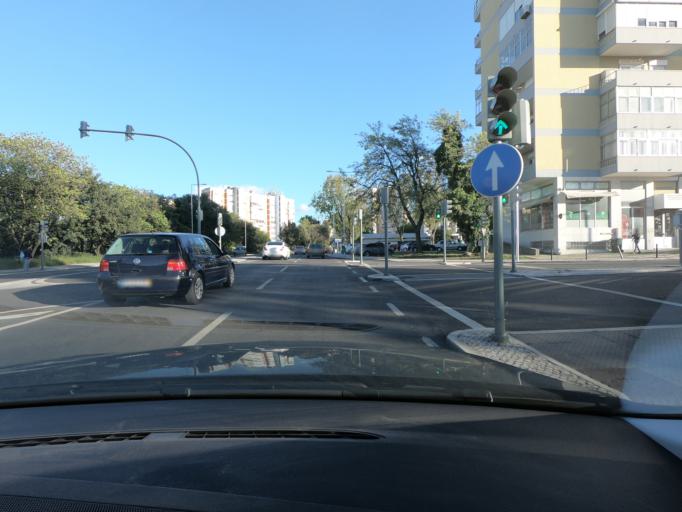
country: PT
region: Lisbon
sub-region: Loures
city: Moscavide
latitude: 38.7656
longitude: -9.1196
